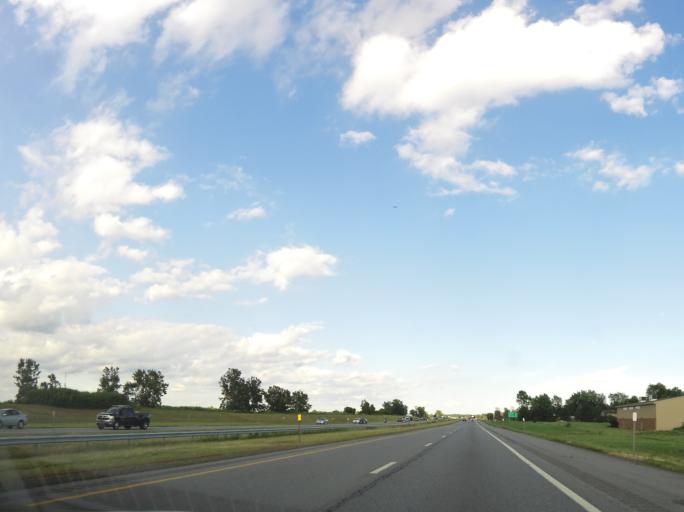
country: US
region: New York
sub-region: Erie County
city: Harris Hill
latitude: 42.9473
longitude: -78.6624
